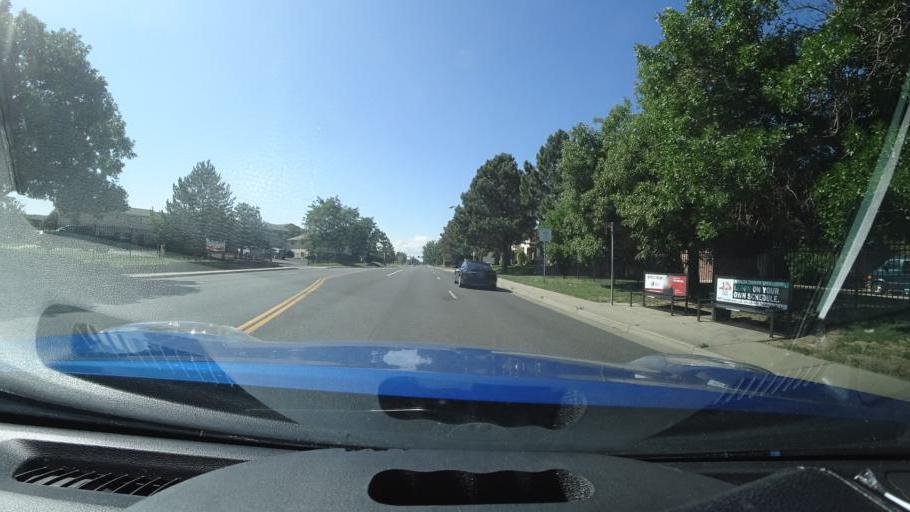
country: US
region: Colorado
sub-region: Adams County
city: Aurora
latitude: 39.6964
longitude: -104.8193
